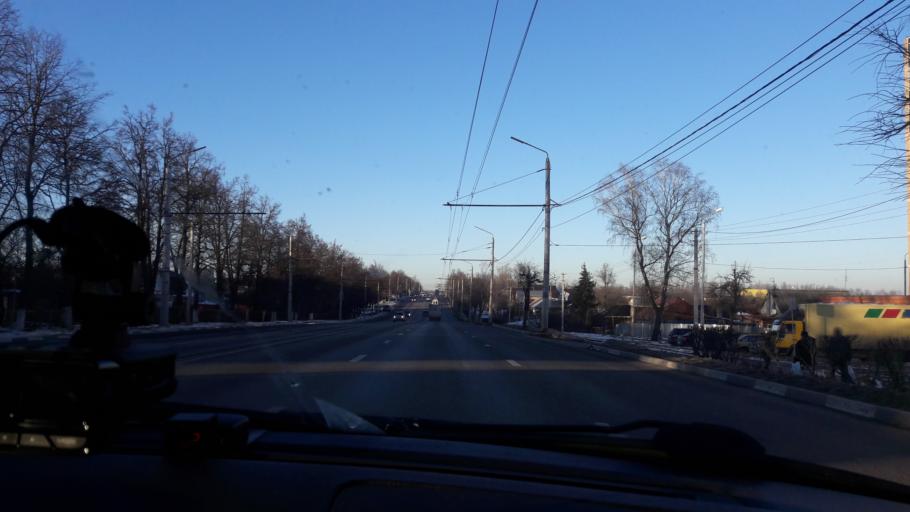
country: RU
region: Tula
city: Gorelki
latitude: 54.2354
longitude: 37.6229
